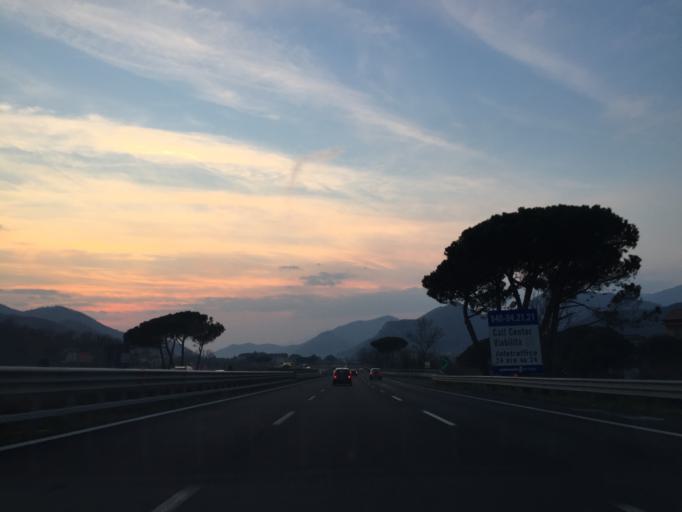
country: IT
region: Campania
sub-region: Provincia di Salerno
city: Faraldo-Nocelleto
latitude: 40.7734
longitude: 14.7678
